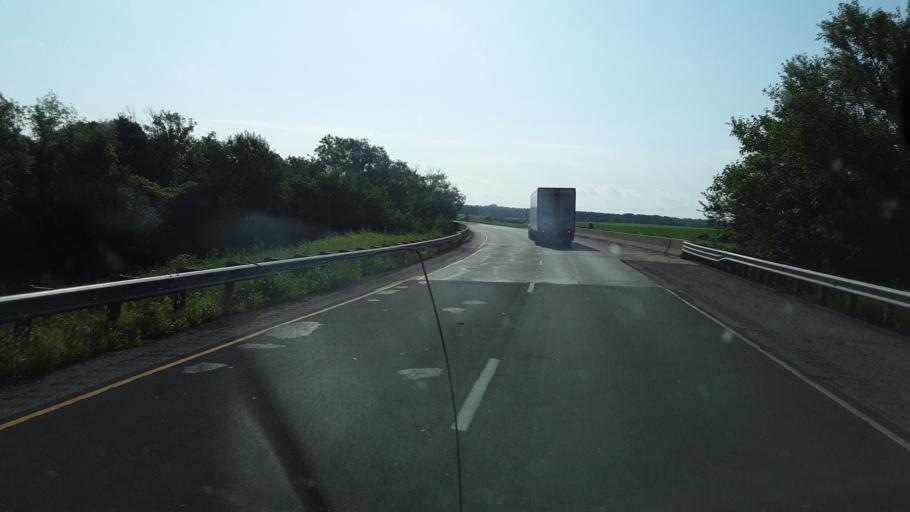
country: US
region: Illinois
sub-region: Madison County
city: Troy
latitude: 38.7515
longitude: -89.9035
